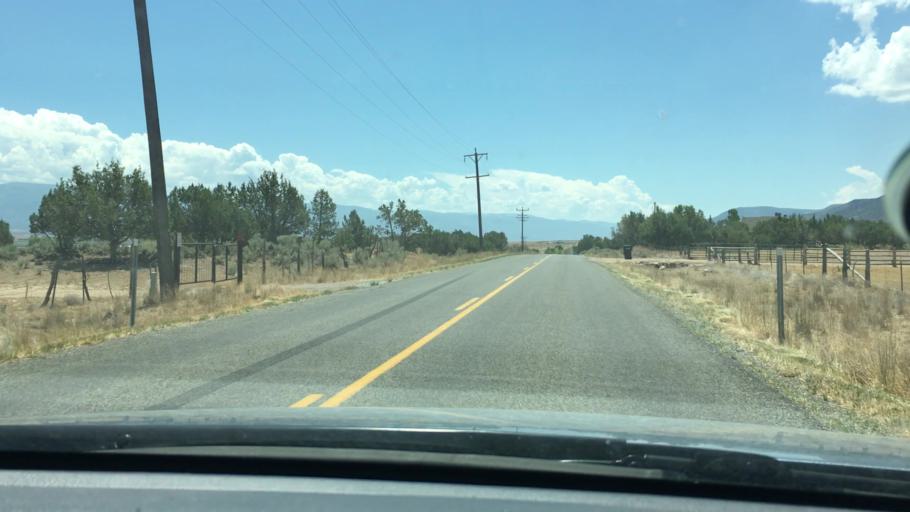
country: US
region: Utah
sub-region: Sanpete County
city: Fountain Green
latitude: 39.5925
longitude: -111.6427
